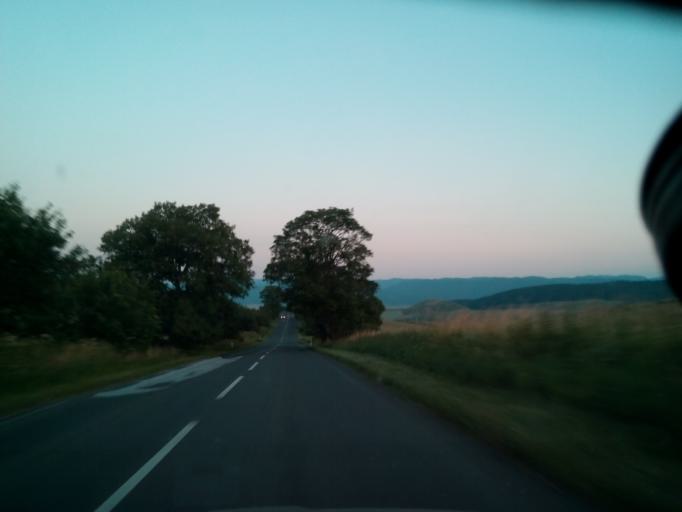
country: SK
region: Presovsky
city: Lubica
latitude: 49.0348
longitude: 20.4362
